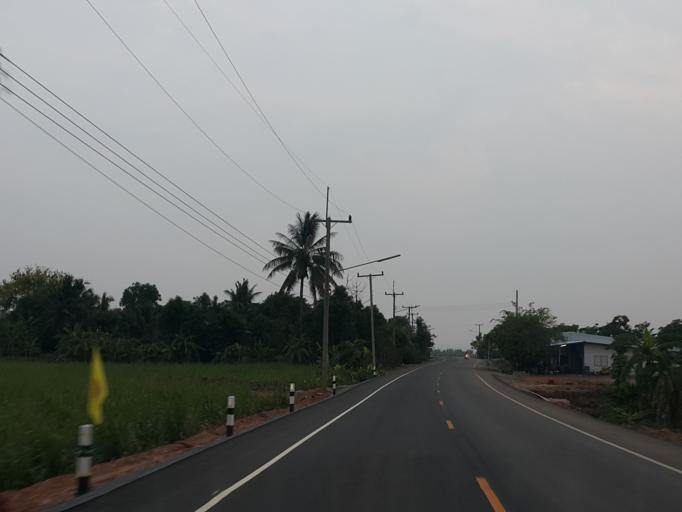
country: TH
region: Suphan Buri
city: Dan Chang
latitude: 14.9365
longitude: 99.6407
